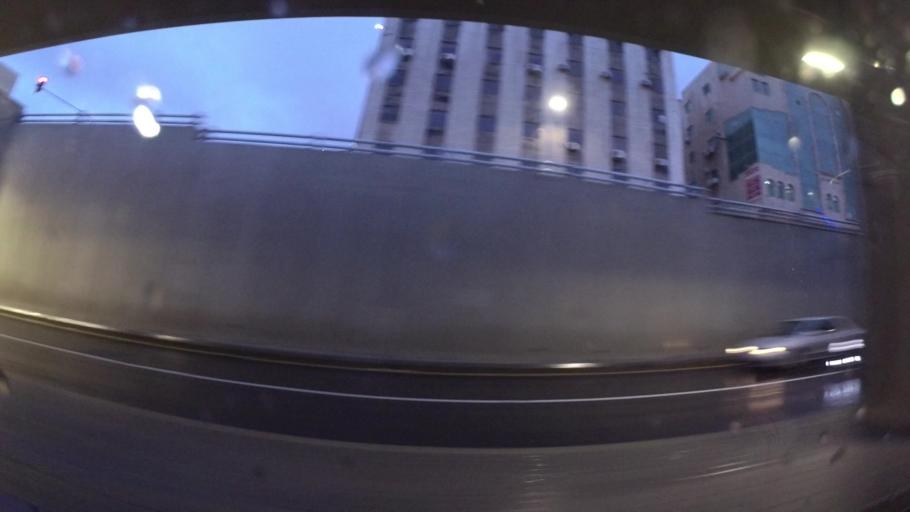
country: JO
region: Amman
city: Al Jubayhah
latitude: 31.9954
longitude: 35.8889
